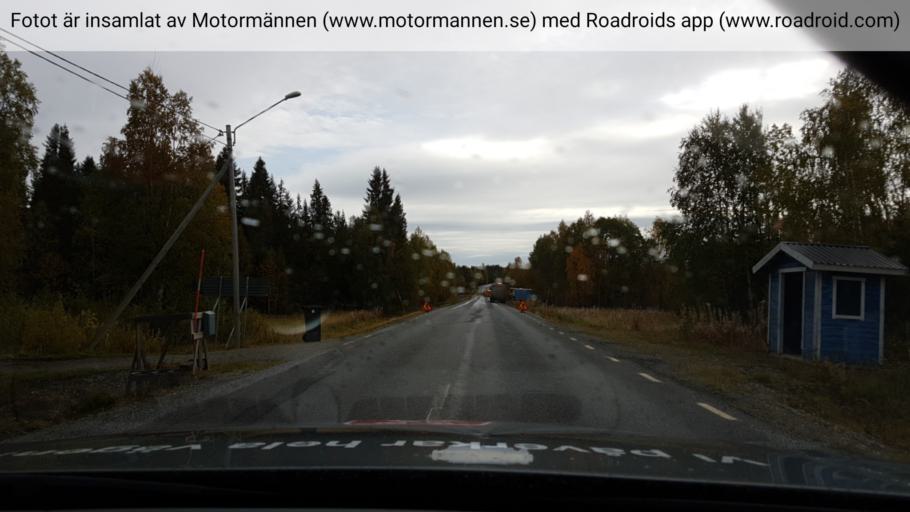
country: SE
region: Vaesterbotten
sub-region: Vilhelmina Kommun
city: Sjoberg
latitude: 64.7661
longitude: 16.1507
